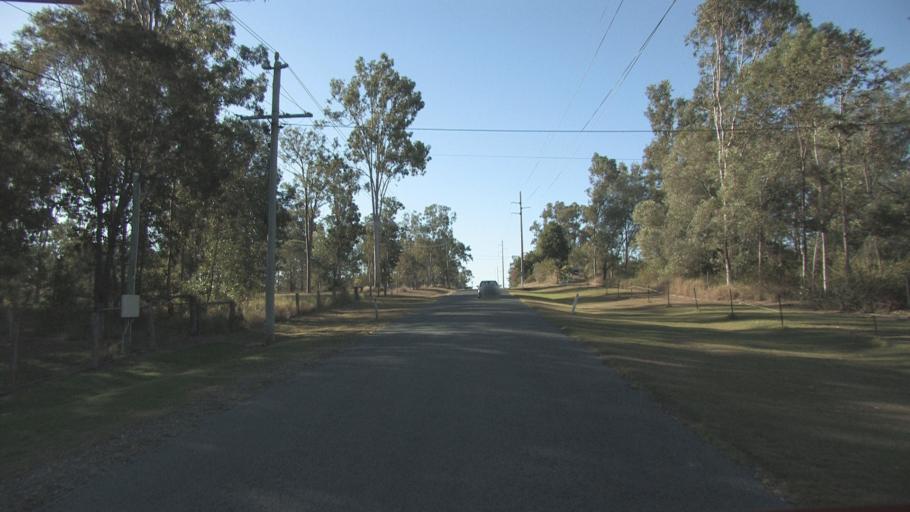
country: AU
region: Queensland
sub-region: Logan
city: North Maclean
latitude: -27.8004
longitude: 153.0412
